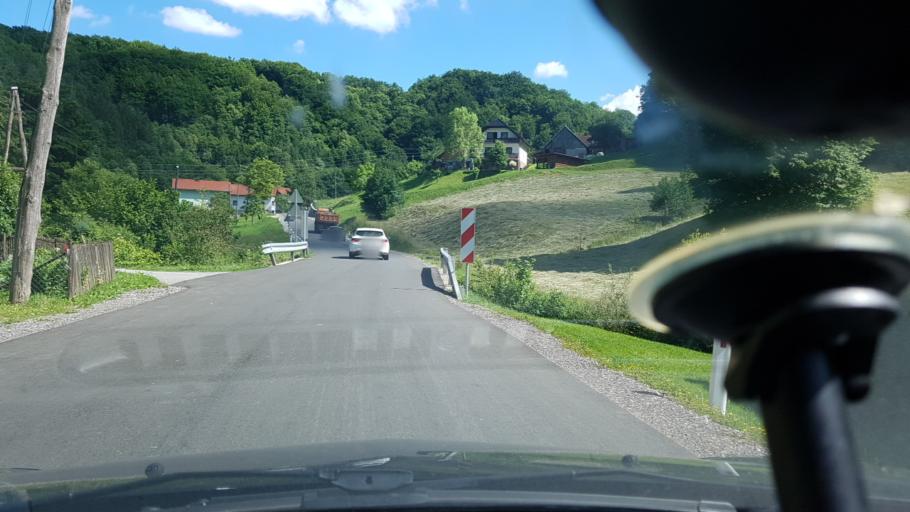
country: SI
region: Zetale
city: Zetale
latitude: 46.2834
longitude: 15.8071
